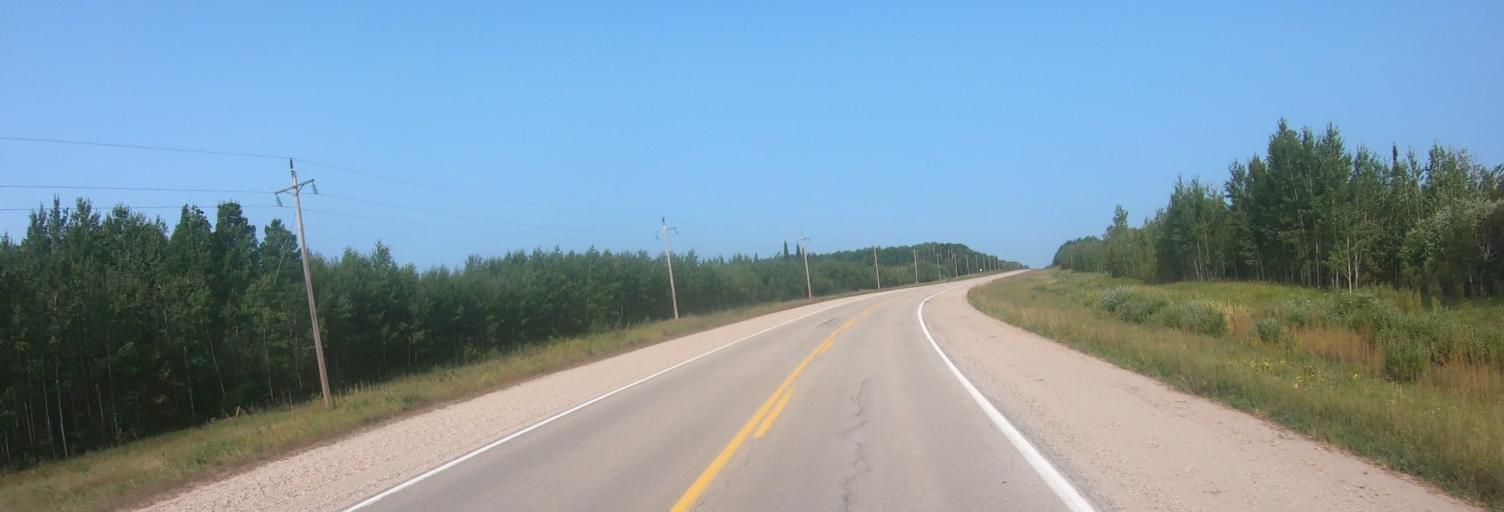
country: US
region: Minnesota
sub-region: Roseau County
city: Roseau
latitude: 49.0237
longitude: -95.7377
